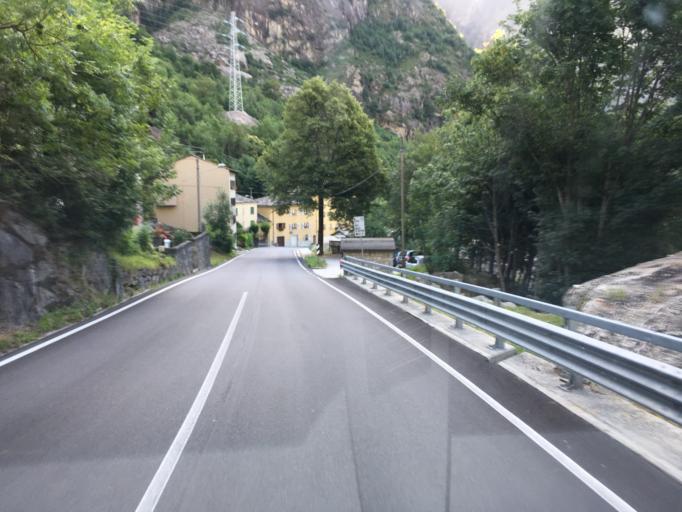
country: IT
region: Lombardy
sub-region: Provincia di Sondrio
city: San Giacomo Filippo
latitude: 46.3692
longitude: 9.3597
